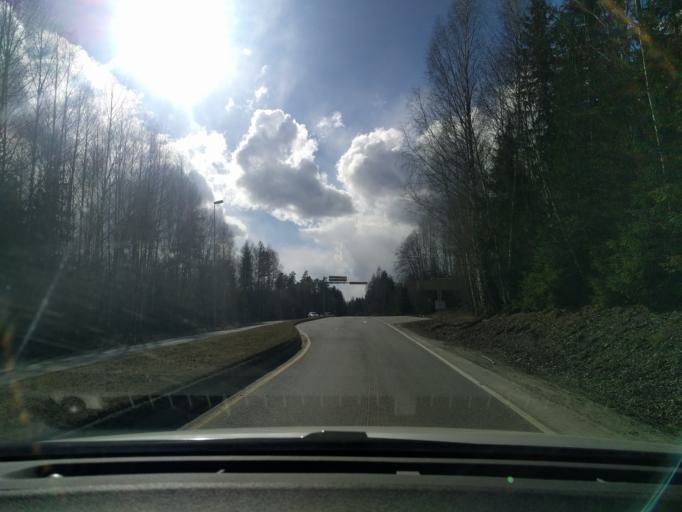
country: NO
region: Hedmark
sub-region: Ringsaker
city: Brumunddal
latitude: 60.8874
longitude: 10.9101
